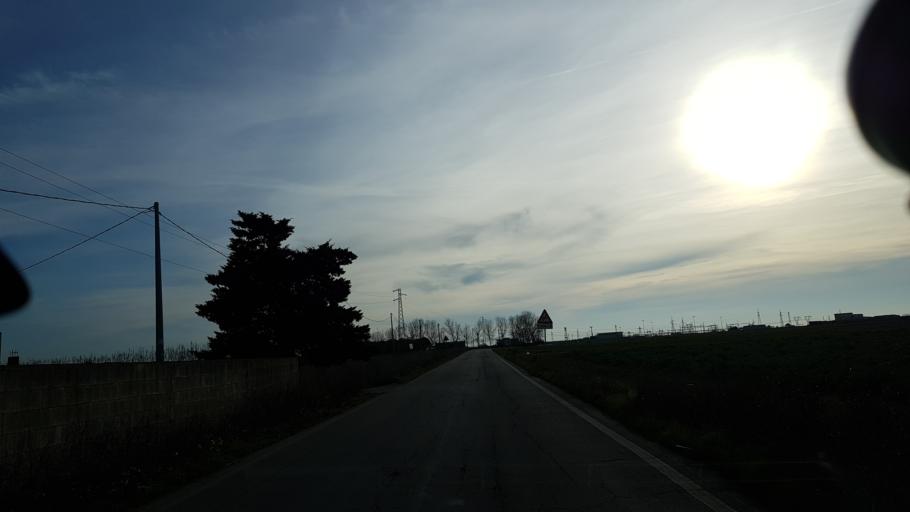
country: IT
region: Apulia
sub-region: Provincia di Brindisi
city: Brindisi
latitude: 40.6106
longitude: 17.9137
